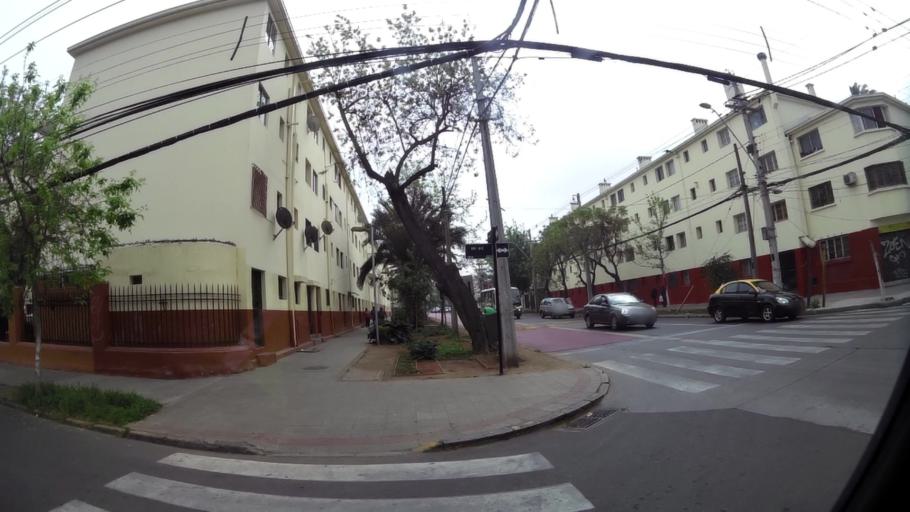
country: CL
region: Santiago Metropolitan
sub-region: Provincia de Santiago
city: Santiago
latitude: -33.4745
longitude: -70.6495
